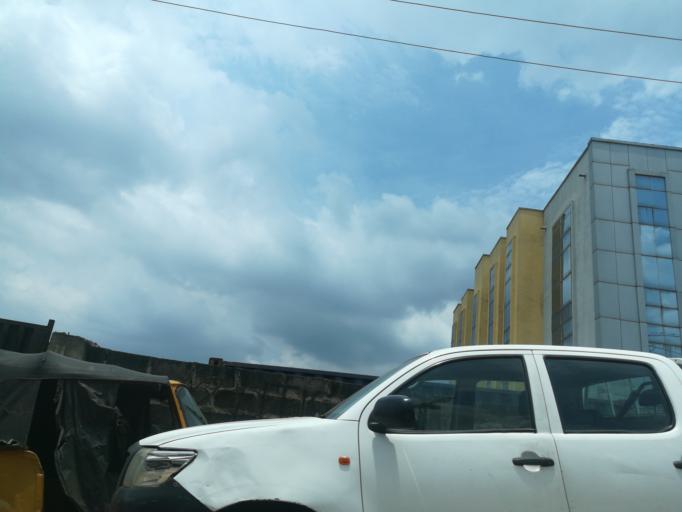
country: NG
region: Lagos
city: Ojota
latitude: 6.5947
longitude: 3.3686
